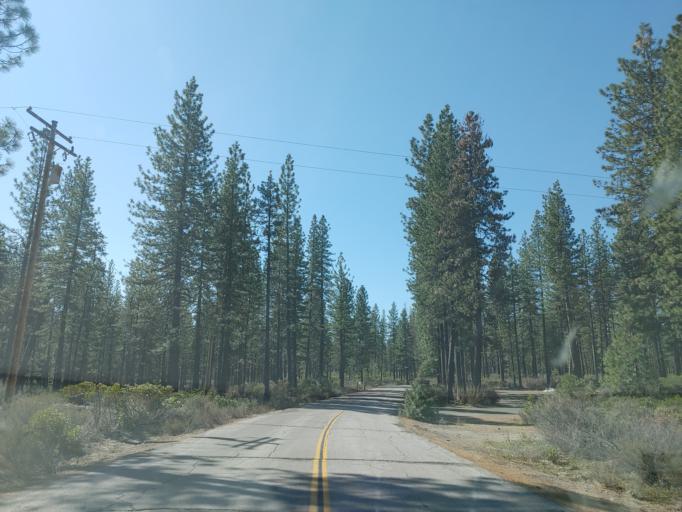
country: US
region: California
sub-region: Siskiyou County
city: McCloud
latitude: 41.2564
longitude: -122.0300
